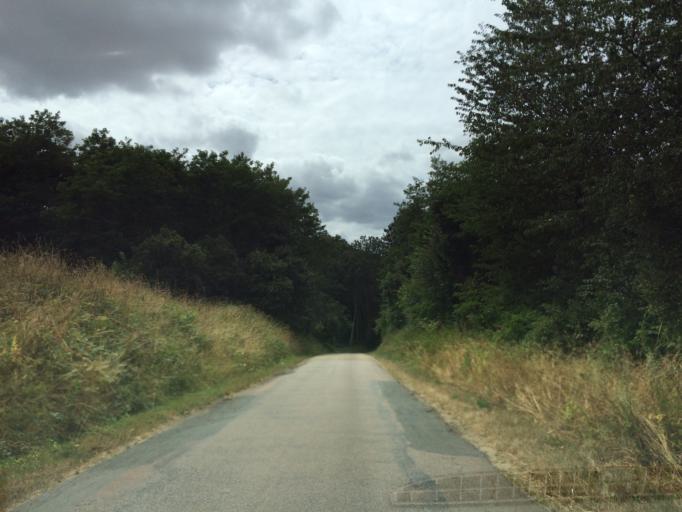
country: FR
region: Bourgogne
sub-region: Departement de l'Yonne
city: Fleury-la-Vallee
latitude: 47.8425
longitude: 3.4086
